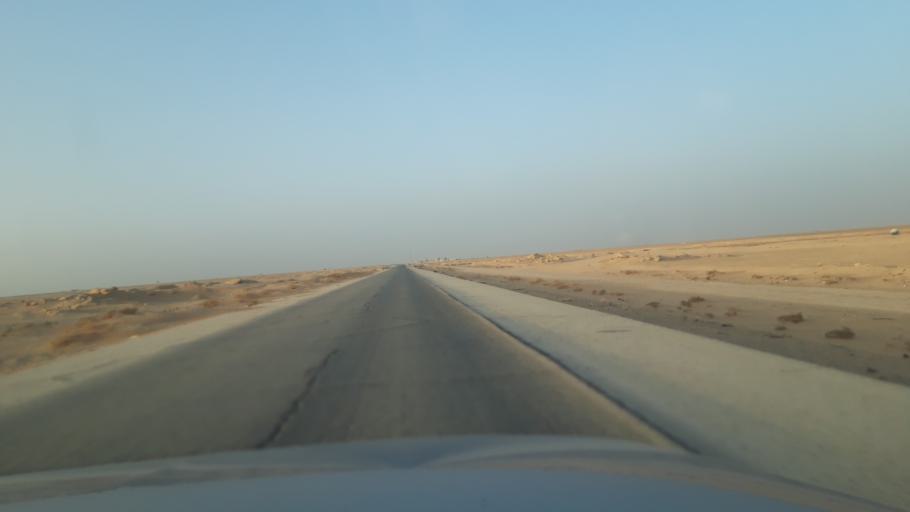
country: JO
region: Ma'an
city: Al Jafr
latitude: 30.2739
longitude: 36.2071
